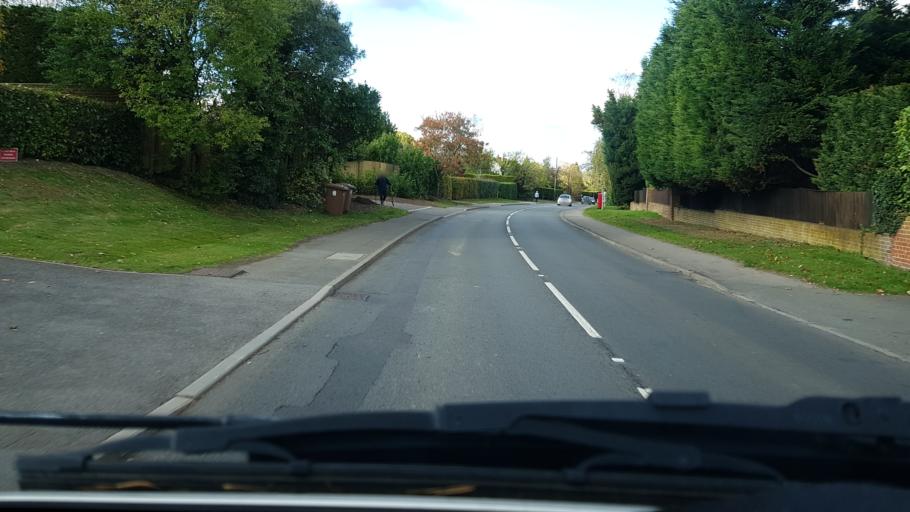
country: GB
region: England
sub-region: Surrey
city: Send
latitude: 51.2644
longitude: -0.5048
